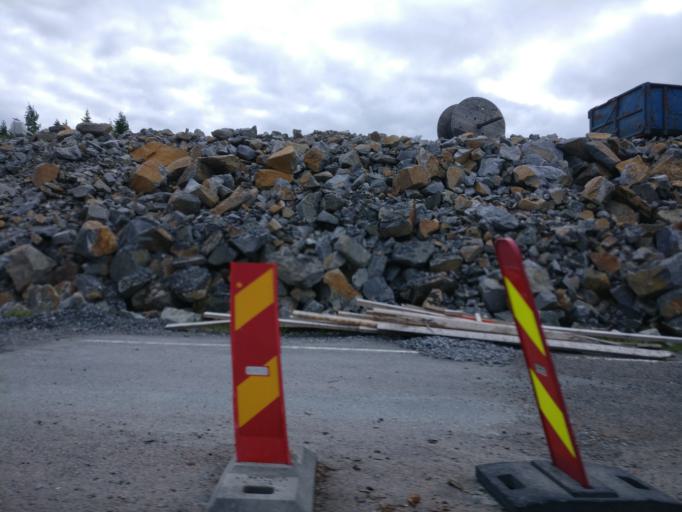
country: FI
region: Northern Savo
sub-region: Kuopio
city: Kuopio
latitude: 62.9721
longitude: 27.8219
